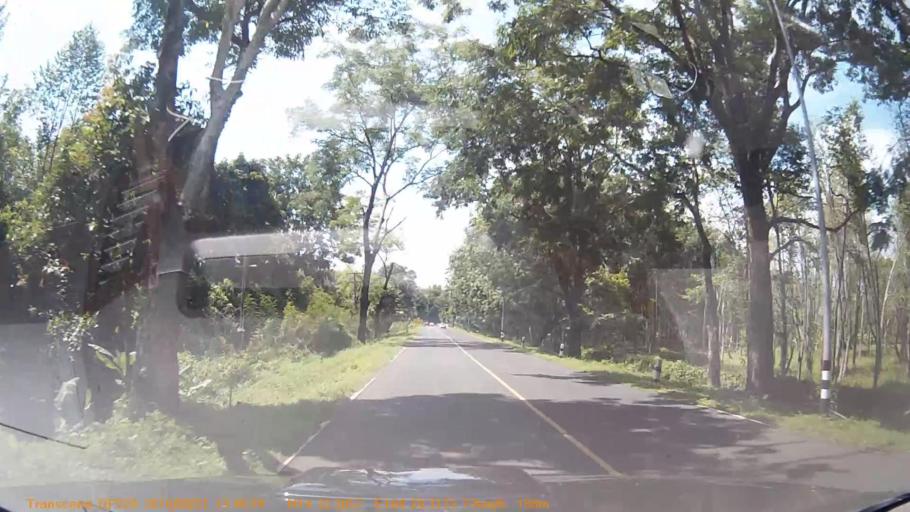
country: TH
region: Sisaket
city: Khun Han
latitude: 14.5390
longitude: 104.4881
